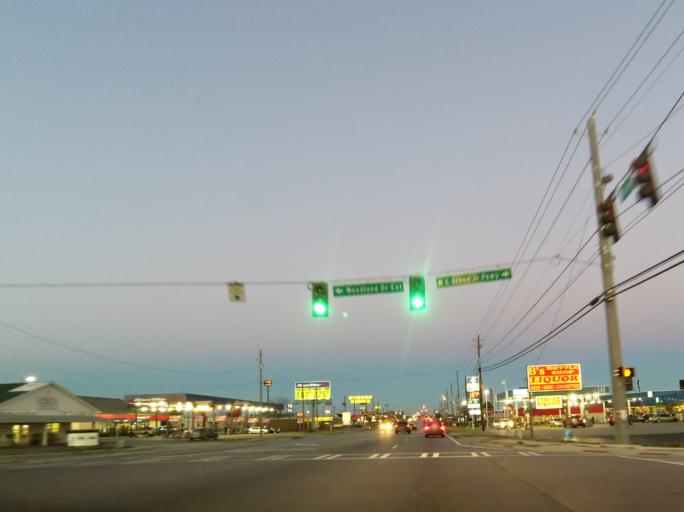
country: US
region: Georgia
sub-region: Peach County
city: Byron
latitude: 32.6568
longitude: -83.7487
